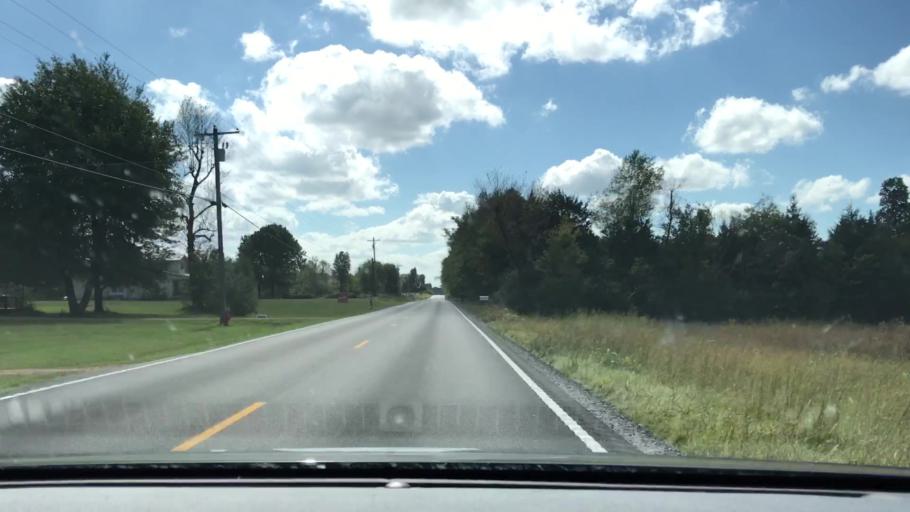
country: US
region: Kentucky
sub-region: Graves County
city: Mayfield
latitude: 36.8002
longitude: -88.5954
